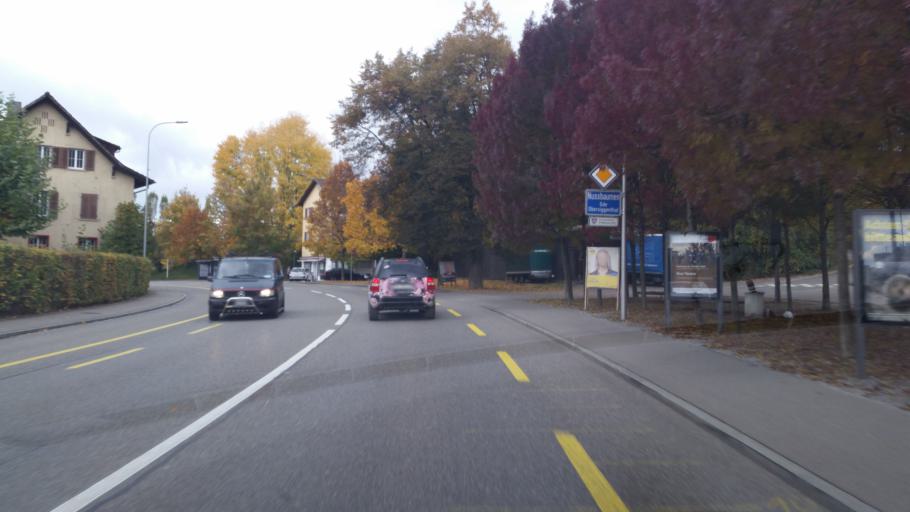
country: CH
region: Aargau
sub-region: Bezirk Baden
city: Obersiggenthal
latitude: 47.4859
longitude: 8.2983
